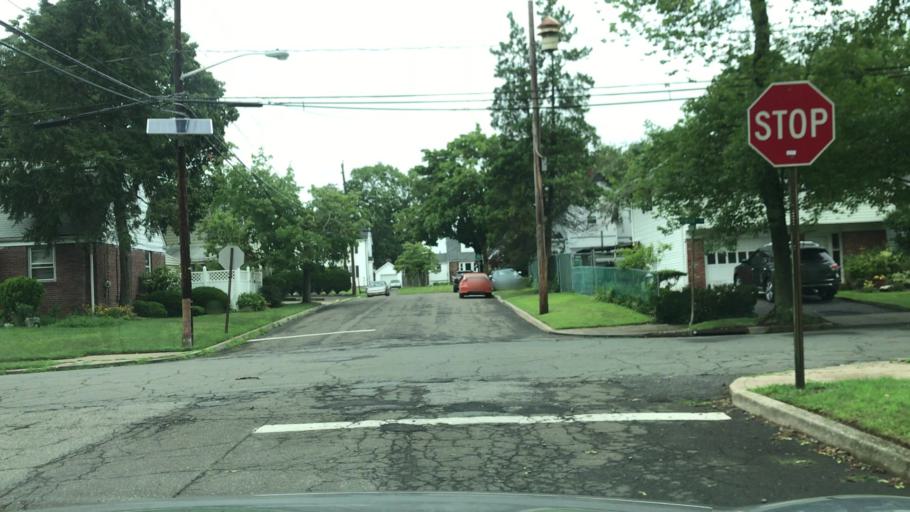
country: US
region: New Jersey
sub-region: Bergen County
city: Bergenfield
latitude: 40.9233
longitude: -73.9890
